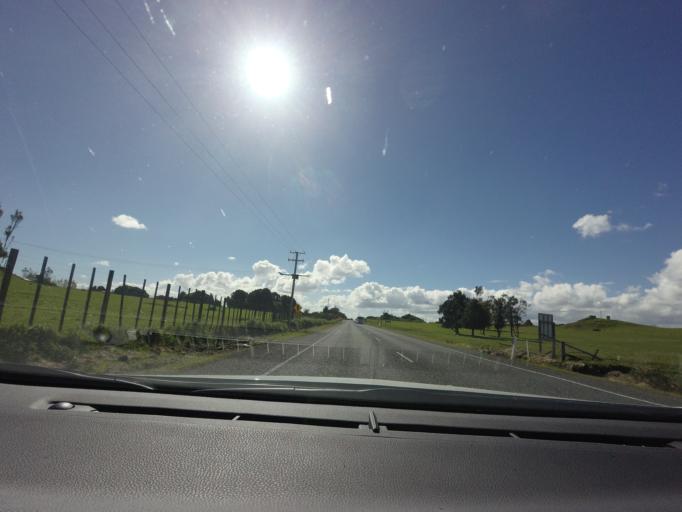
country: NZ
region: Bay of Plenty
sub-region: Rotorua District
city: Rotorua
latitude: -38.0516
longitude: 176.0791
